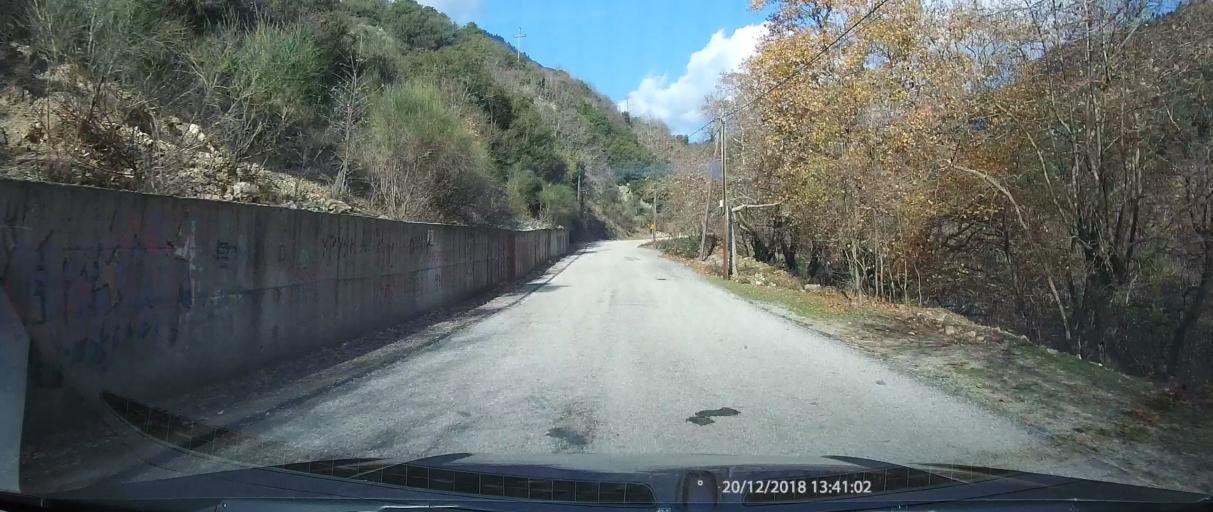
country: GR
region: West Greece
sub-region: Nomos Aitolias kai Akarnanias
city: Thermo
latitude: 38.6457
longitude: 21.6134
